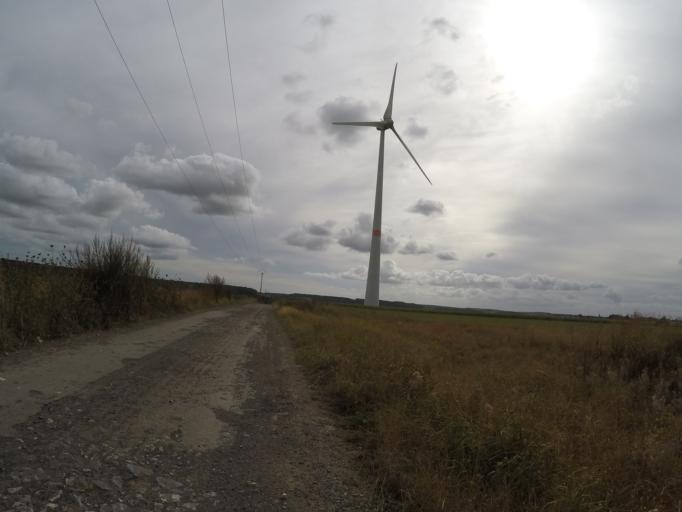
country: BE
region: Wallonia
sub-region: Province de Namur
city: Dinant
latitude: 50.2958
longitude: 4.9836
